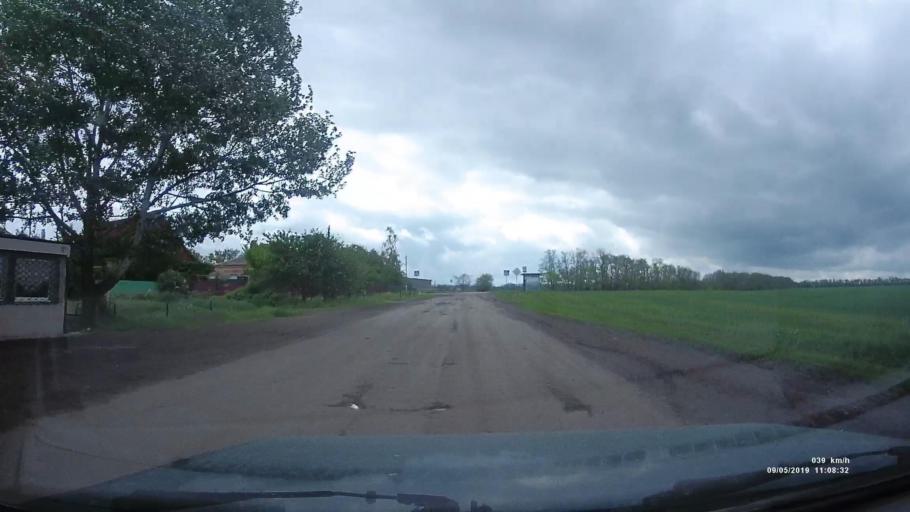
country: RU
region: Krasnodarskiy
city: Kanelovskaya
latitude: 46.7888
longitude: 39.2100
